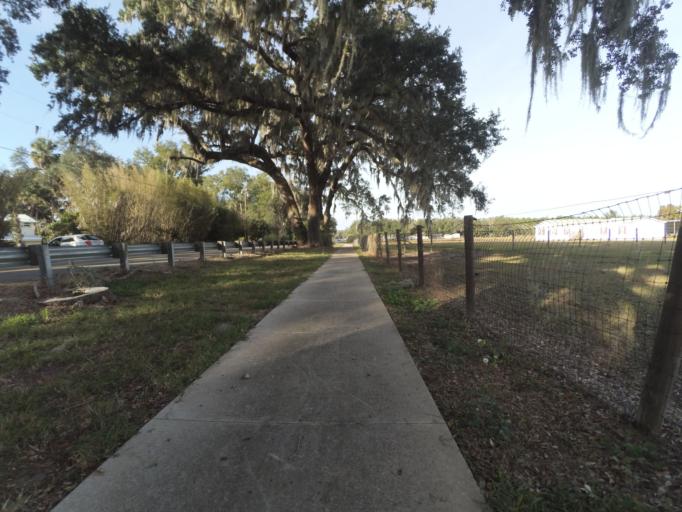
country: US
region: Florida
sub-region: Lake County
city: Umatilla
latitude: 28.9640
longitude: -81.6367
